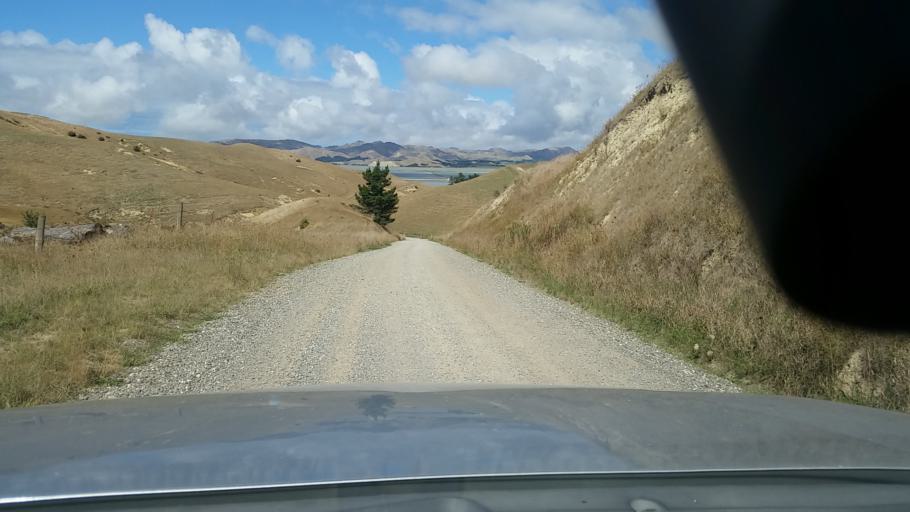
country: NZ
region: Marlborough
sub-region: Marlborough District
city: Blenheim
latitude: -41.6954
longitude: 174.1464
